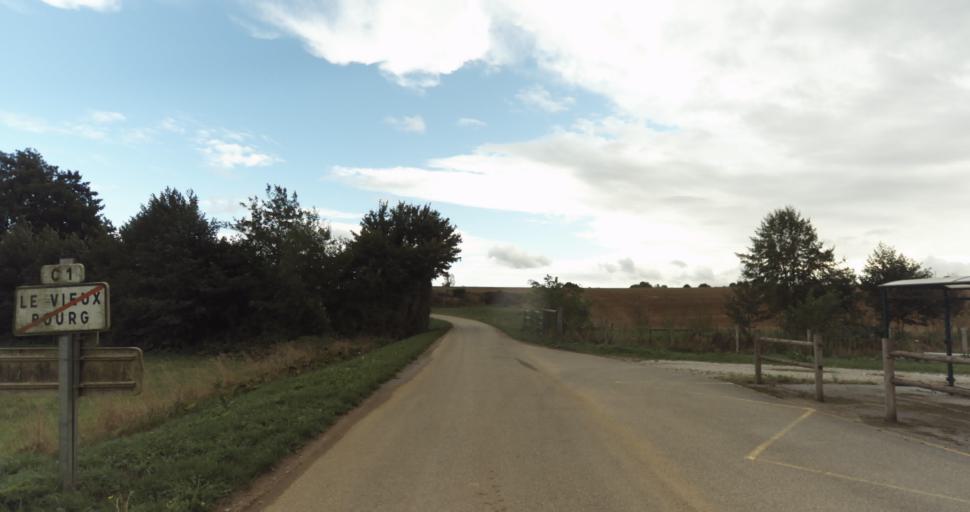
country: FR
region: Lower Normandy
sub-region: Departement de l'Orne
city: Sainte-Gauburge-Sainte-Colombe
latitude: 48.7377
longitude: 0.4057
